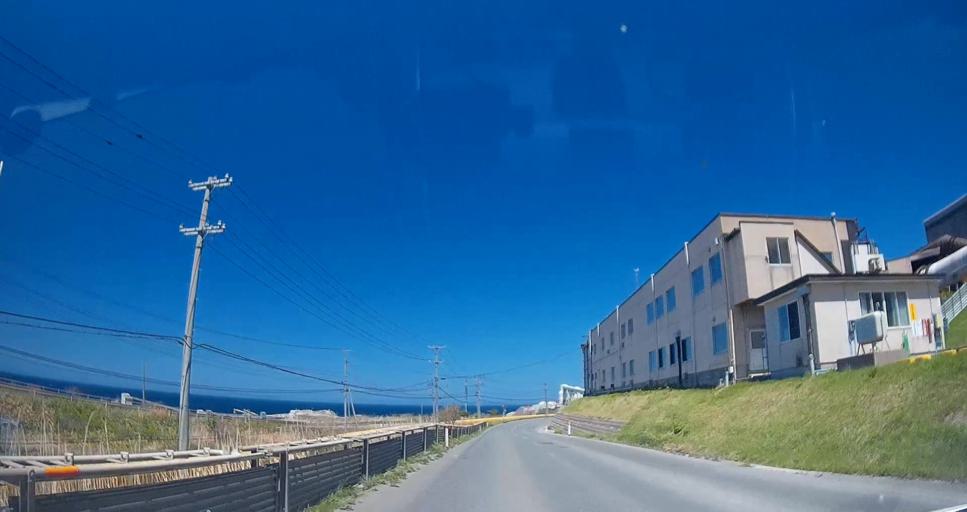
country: JP
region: Aomori
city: Mutsu
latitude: 41.4066
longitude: 141.4360
